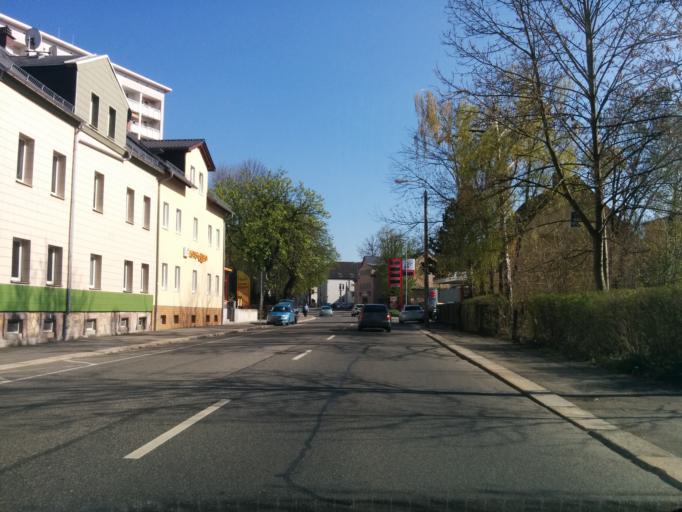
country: DE
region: Saxony
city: Hilbersdorf
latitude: 50.8314
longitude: 12.9573
